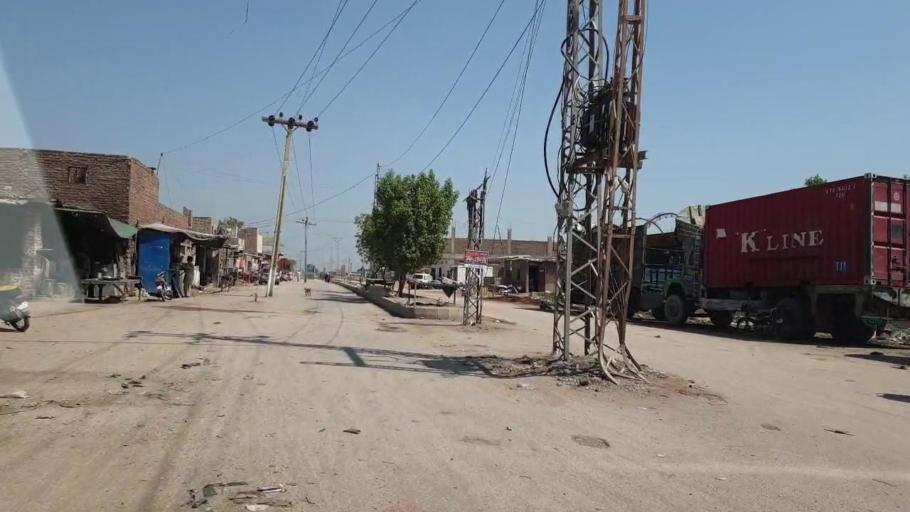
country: PK
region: Sindh
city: Hyderabad
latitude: 25.4165
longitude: 68.3840
